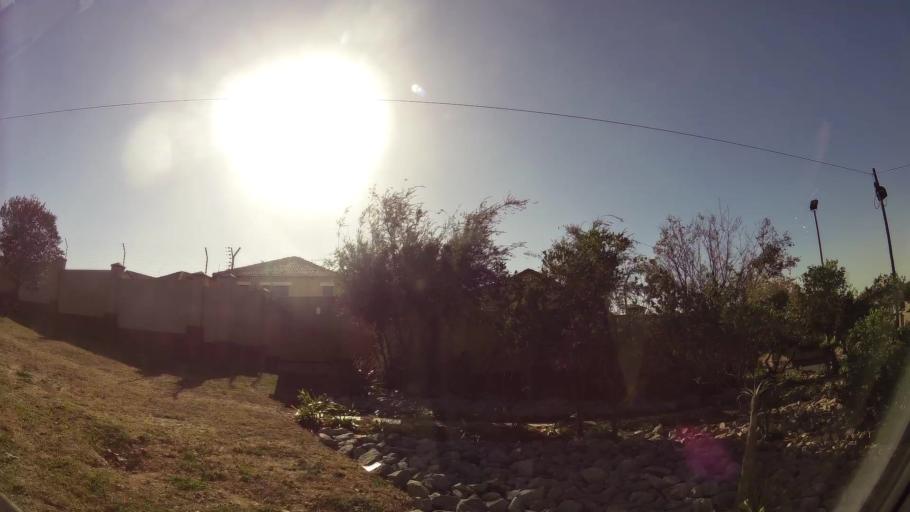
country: ZA
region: Gauteng
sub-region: City of Johannesburg Metropolitan Municipality
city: Diepsloot
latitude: -26.0235
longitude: 27.9738
